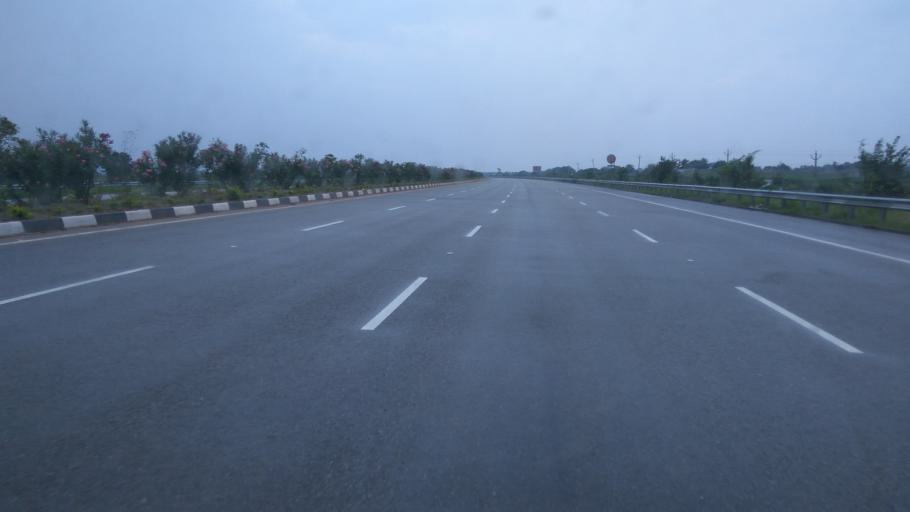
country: IN
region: Telangana
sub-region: Rangareddi
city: Ghatkesar
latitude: 17.4757
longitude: 78.6695
